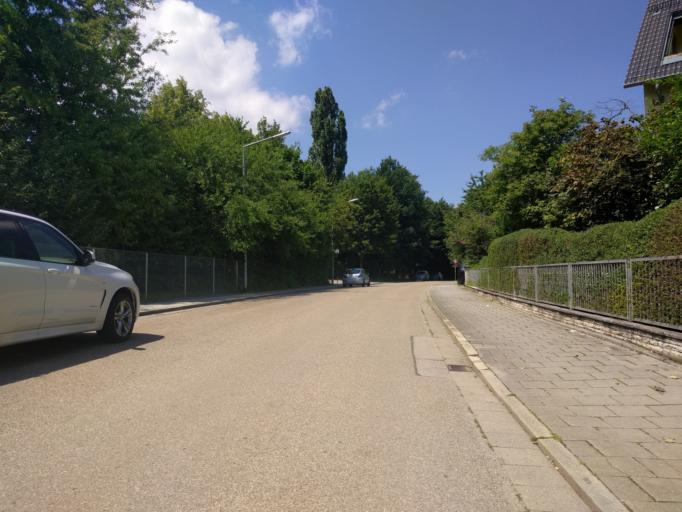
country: DE
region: Bavaria
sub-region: Upper Palatinate
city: Pentling
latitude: 49.0026
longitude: 12.0779
